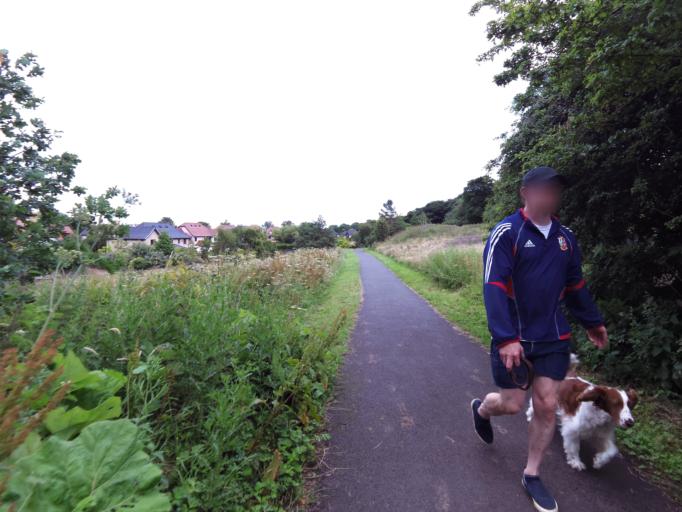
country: GB
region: Scotland
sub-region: East Lothian
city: Musselburgh
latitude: 55.9448
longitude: -3.0835
